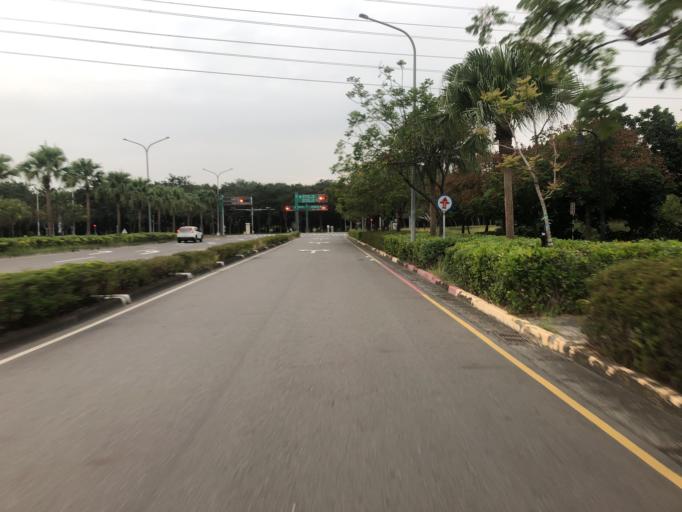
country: TW
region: Taiwan
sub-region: Tainan
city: Tainan
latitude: 23.1016
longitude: 120.2766
